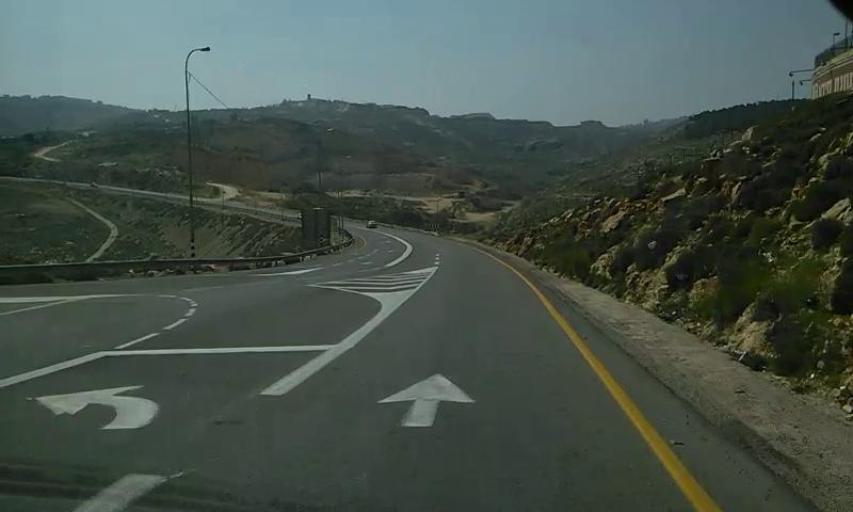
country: PS
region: West Bank
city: Jaba`
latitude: 31.8718
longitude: 35.2601
